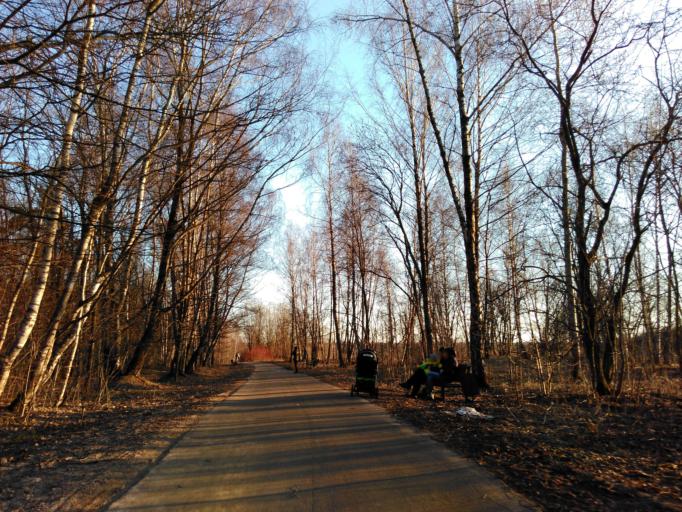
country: RU
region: Moscow
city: Zyuzino
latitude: 55.6354
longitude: 37.5620
